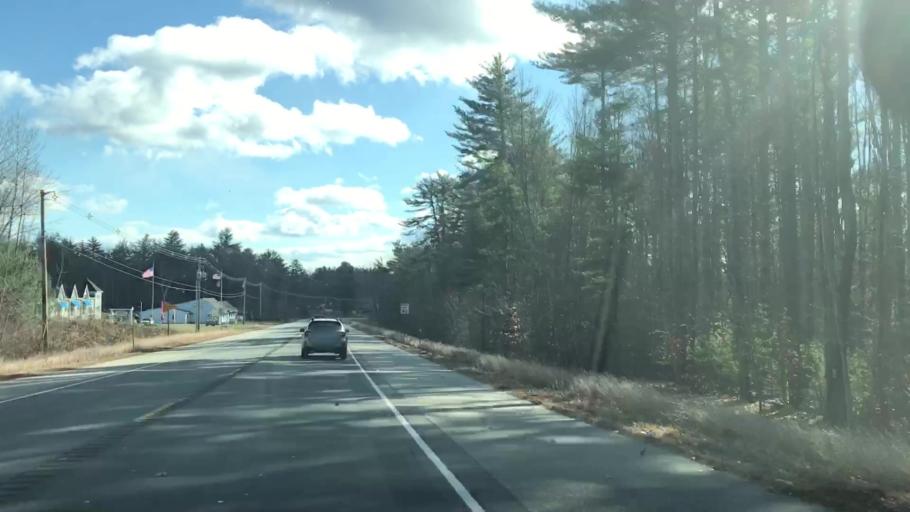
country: US
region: New Hampshire
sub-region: Strafford County
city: New Durham
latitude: 43.4591
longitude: -71.2185
